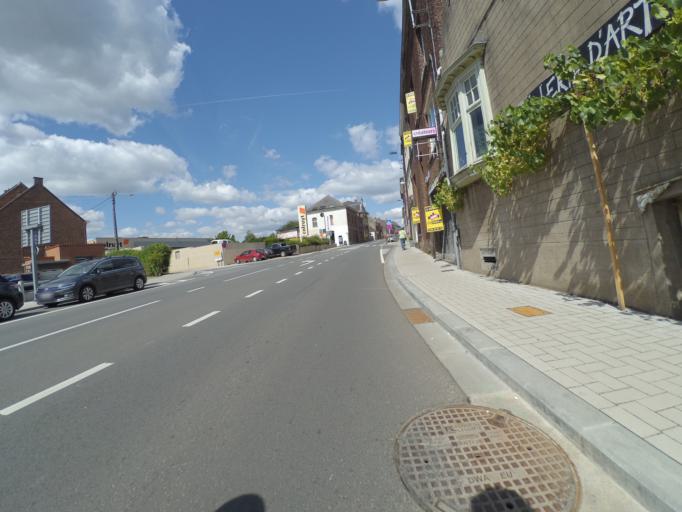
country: BE
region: Wallonia
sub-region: Province du Hainaut
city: Ellezelles
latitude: 50.7325
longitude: 3.6820
